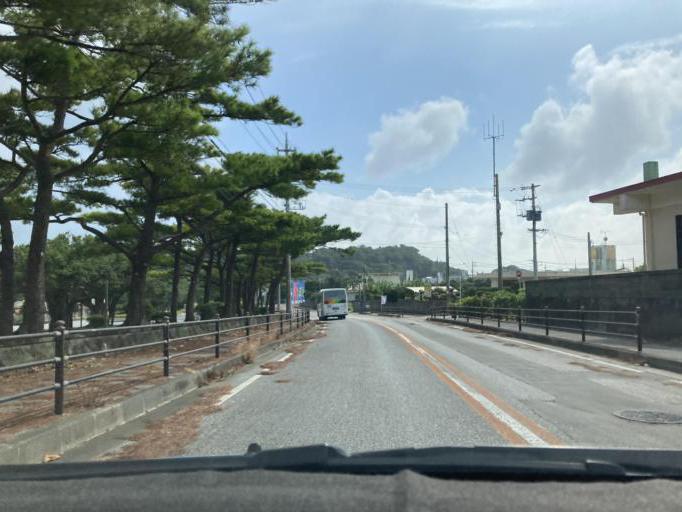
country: JP
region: Okinawa
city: Itoman
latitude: 26.0967
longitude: 127.7216
